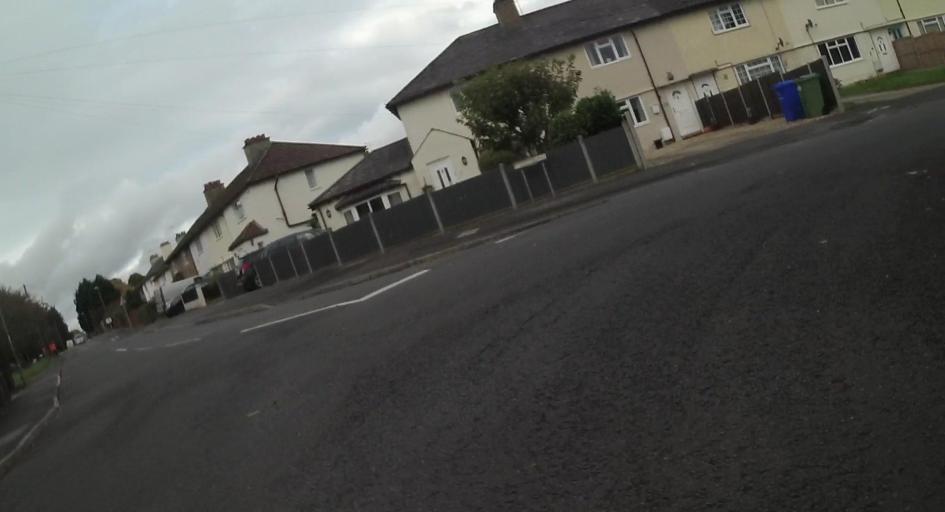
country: GB
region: England
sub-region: Hampshire
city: Farnborough
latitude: 51.2861
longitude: -0.7719
